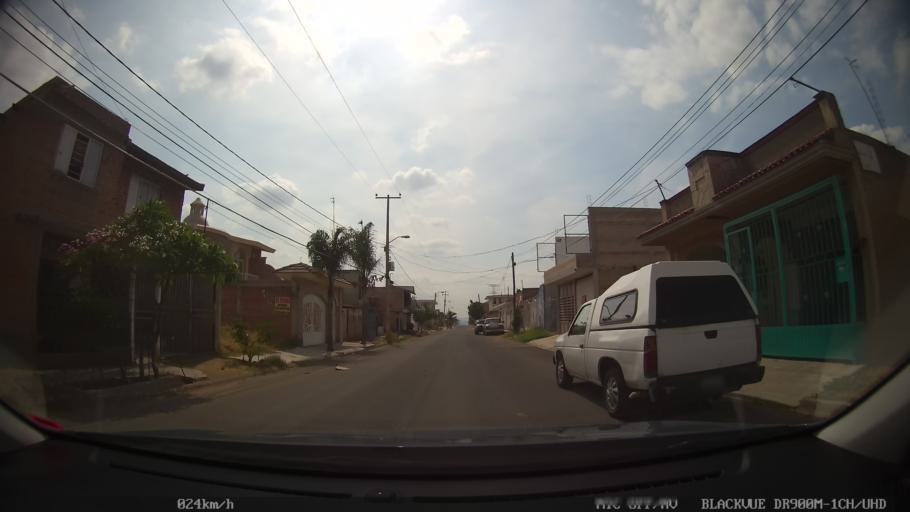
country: MX
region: Jalisco
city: Coyula
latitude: 20.6468
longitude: -103.2123
